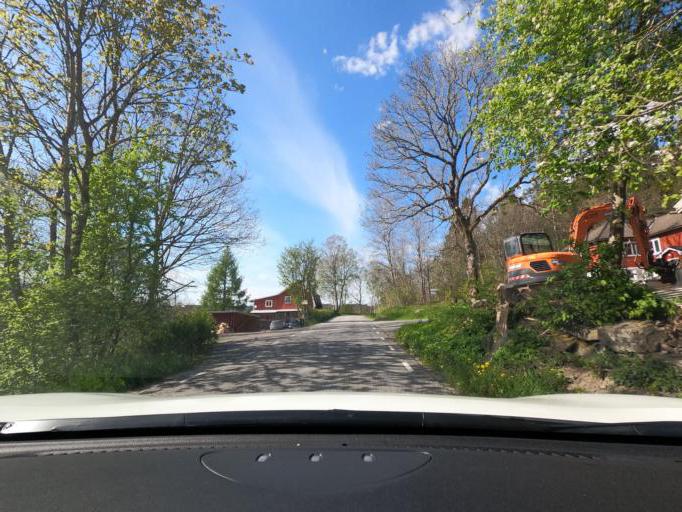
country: SE
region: Vaestra Goetaland
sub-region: Harryda Kommun
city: Ravlanda
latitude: 57.6316
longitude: 12.4980
